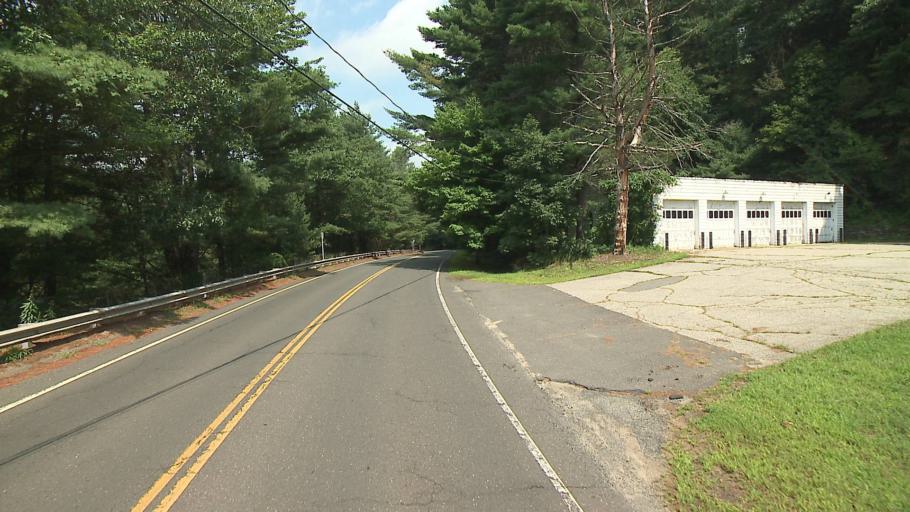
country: US
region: Connecticut
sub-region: Litchfield County
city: Thomaston
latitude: 41.6657
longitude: -73.1318
